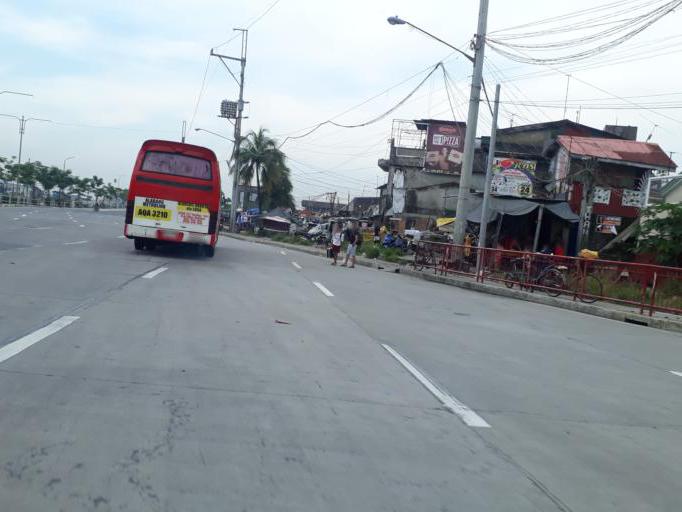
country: PH
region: Metro Manila
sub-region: Caloocan City
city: Niugan
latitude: 14.6480
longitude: 120.9501
